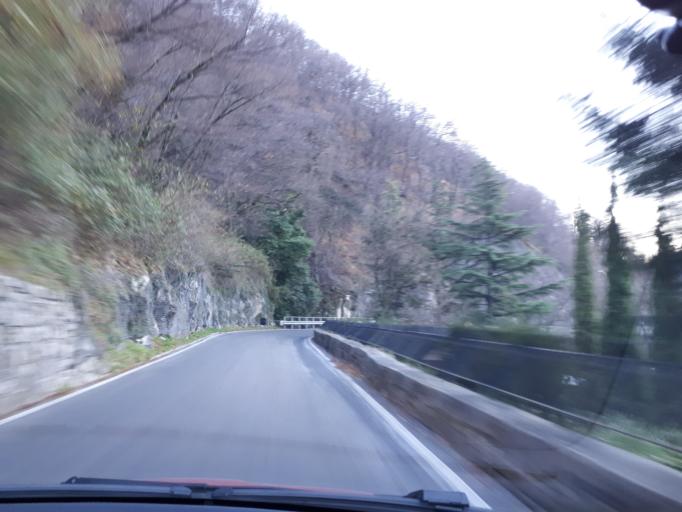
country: IT
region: Lombardy
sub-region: Provincia di Como
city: Nesso
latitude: 45.9316
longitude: 9.1509
